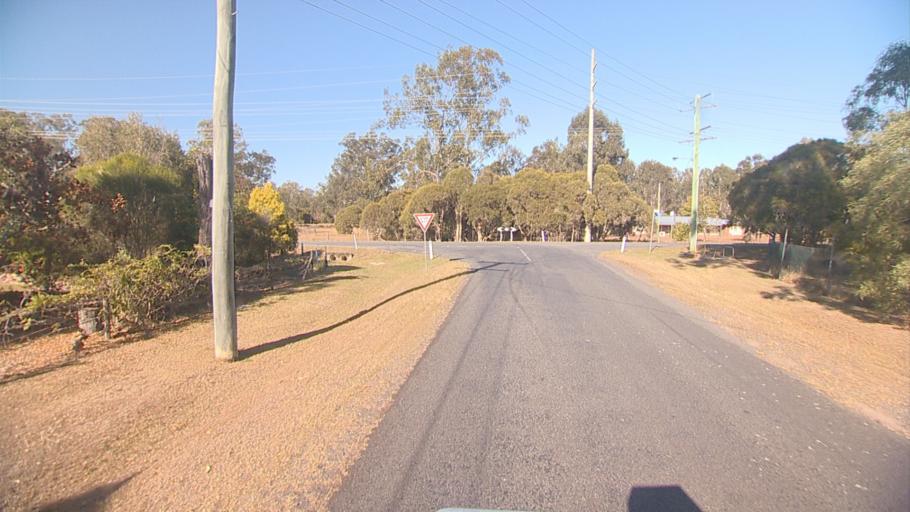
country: AU
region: Queensland
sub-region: Logan
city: Cedar Vale
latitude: -27.8404
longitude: 153.0311
